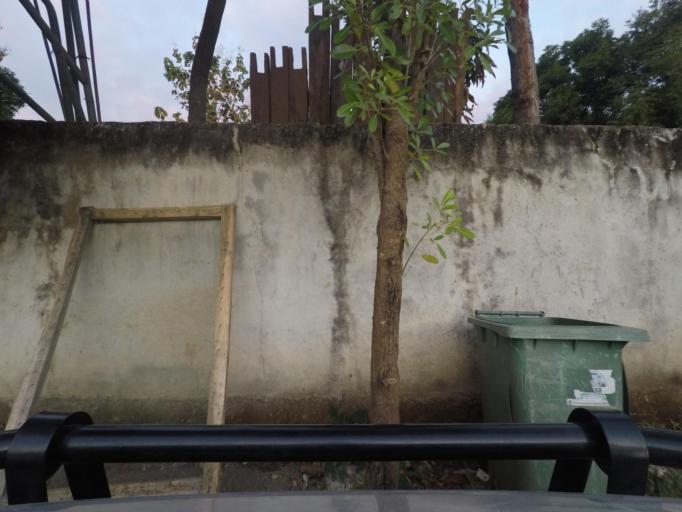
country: TL
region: Bobonaro
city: Maliana
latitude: -8.9874
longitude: 125.2102
